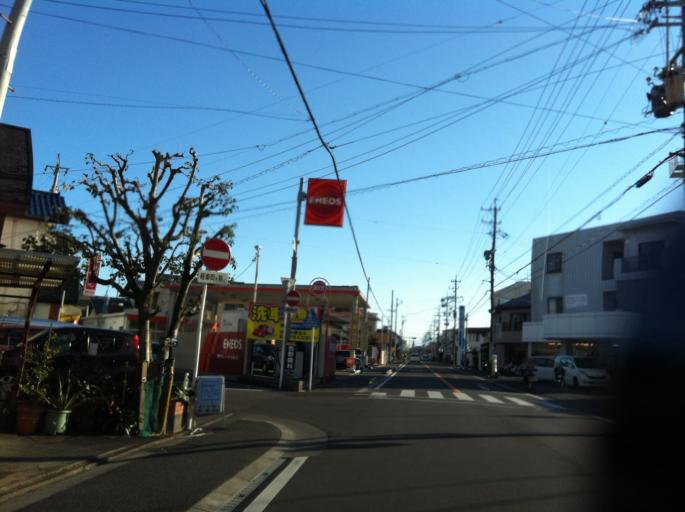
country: JP
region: Shizuoka
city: Shizuoka-shi
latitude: 34.9986
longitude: 138.3831
